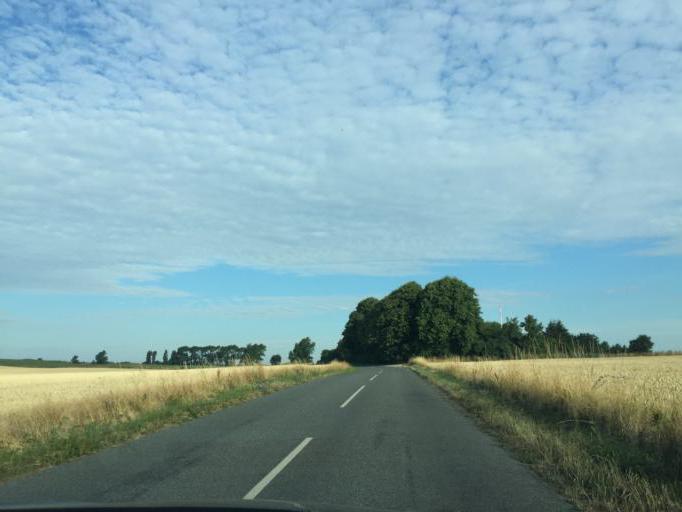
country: DK
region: South Denmark
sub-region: Assens Kommune
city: Harby
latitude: 55.1574
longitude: 10.0015
